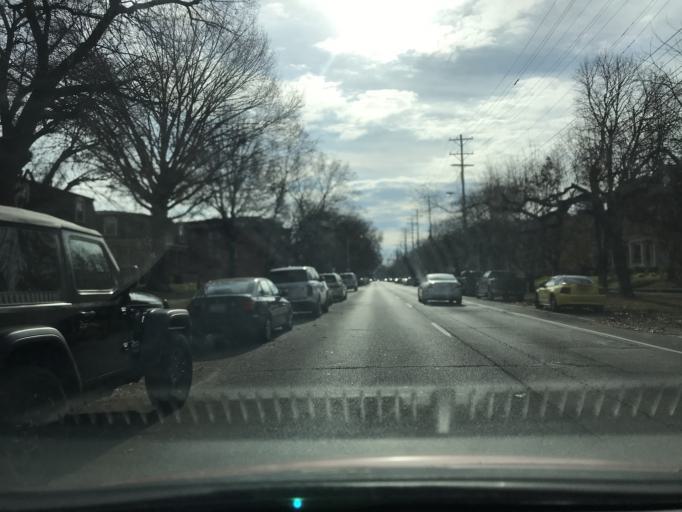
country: US
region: Kentucky
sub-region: Jefferson County
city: Louisville
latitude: 38.2253
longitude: -85.7604
